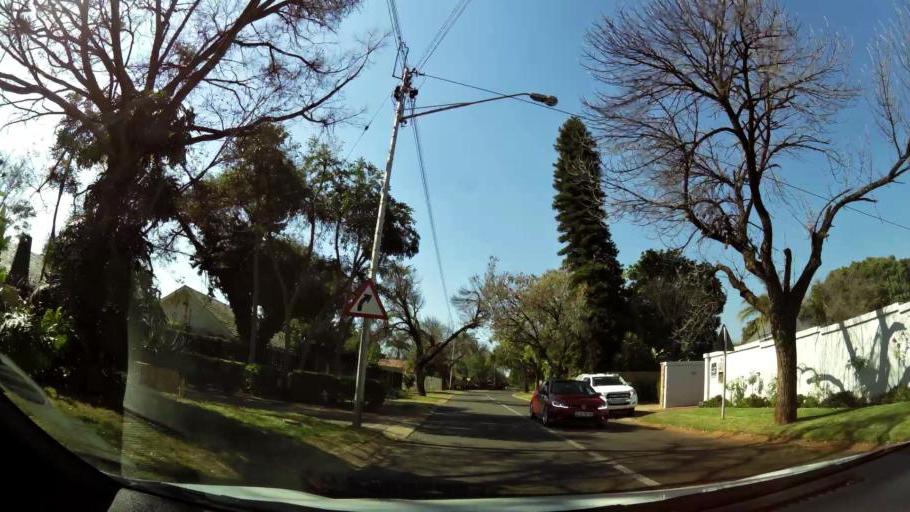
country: ZA
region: Gauteng
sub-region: City of Tshwane Metropolitan Municipality
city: Pretoria
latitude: -25.7616
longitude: 28.2603
